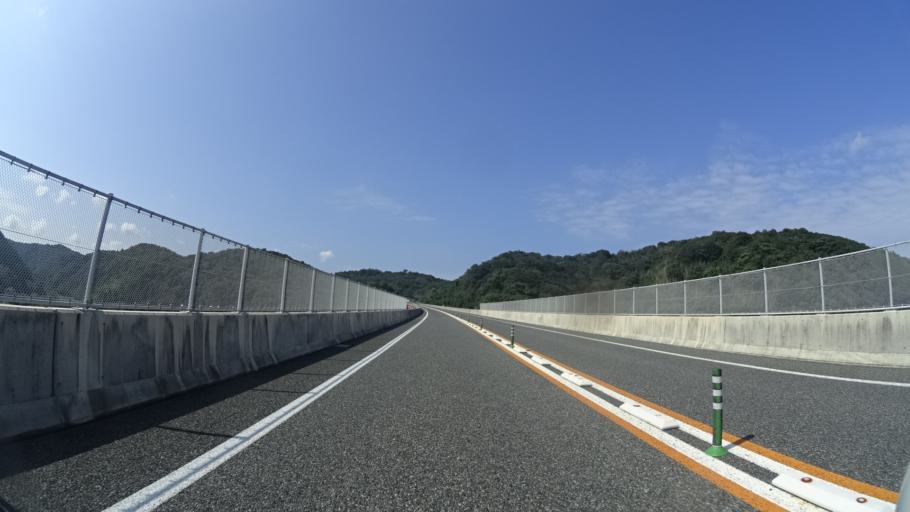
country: JP
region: Shimane
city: Gotsucho
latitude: 34.9688
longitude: 132.1717
